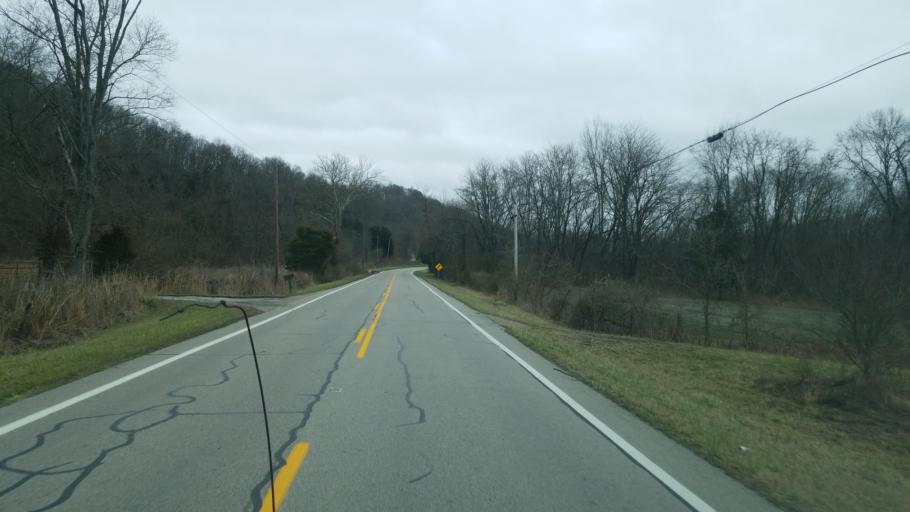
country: US
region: Kentucky
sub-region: Bracken County
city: Brooksville
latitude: 38.8036
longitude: -84.1876
